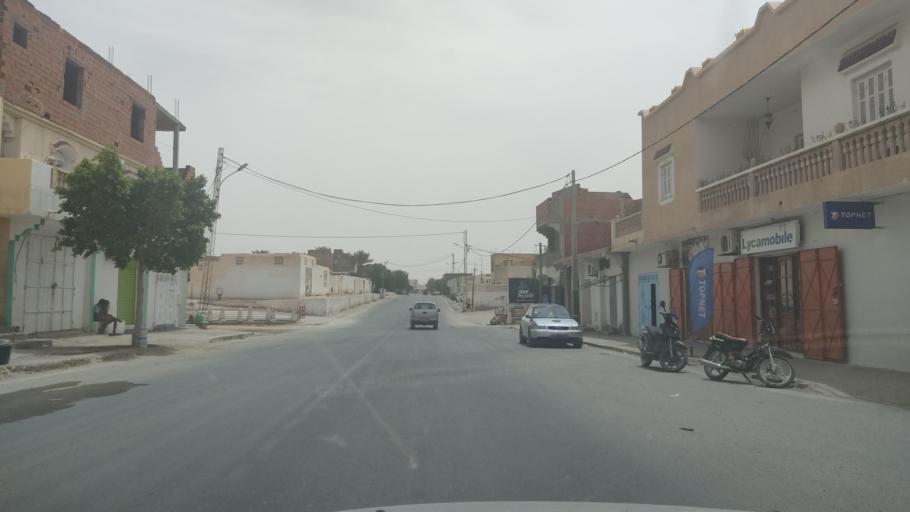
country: TN
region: Gafsa
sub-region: Gafsa Municipality
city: Gafsa
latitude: 34.3389
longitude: 8.9524
